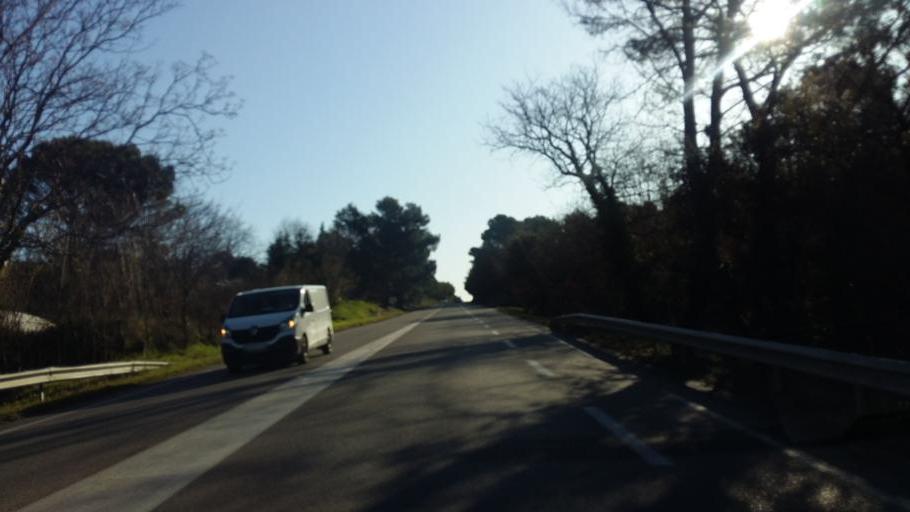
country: FR
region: Provence-Alpes-Cote d'Azur
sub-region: Departement des Bouches-du-Rhone
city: Mallemort
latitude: 43.7133
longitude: 5.1960
